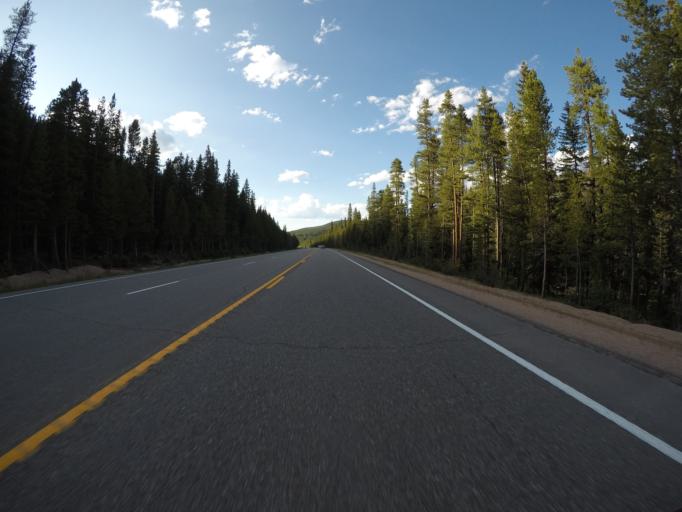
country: US
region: Colorado
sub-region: Grand County
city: Fraser
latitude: 39.8707
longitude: -105.7505
